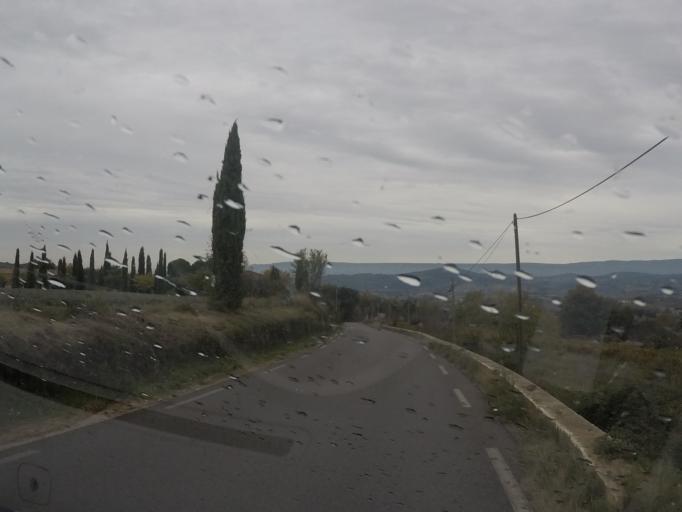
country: FR
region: Provence-Alpes-Cote d'Azur
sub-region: Departement du Vaucluse
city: Bonnieux
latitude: 43.8303
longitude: 5.2975
